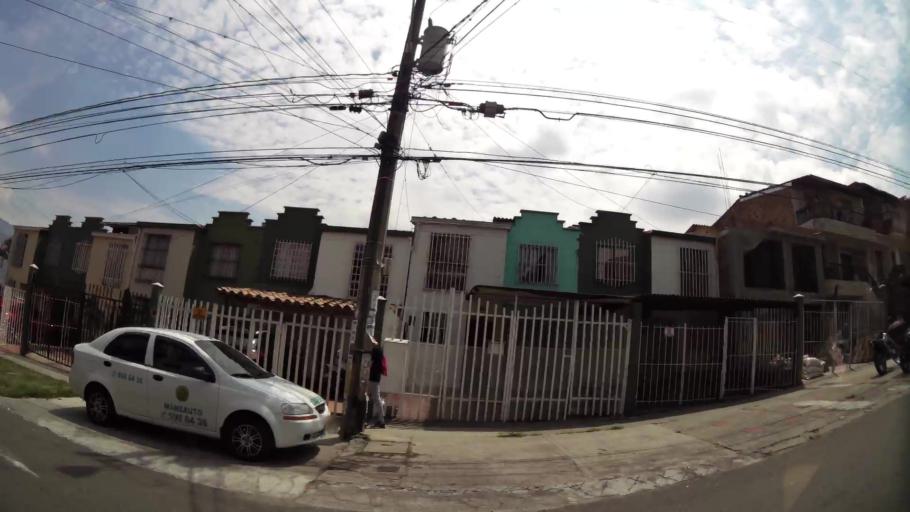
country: CO
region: Antioquia
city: Bello
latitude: 6.3149
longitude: -75.5636
